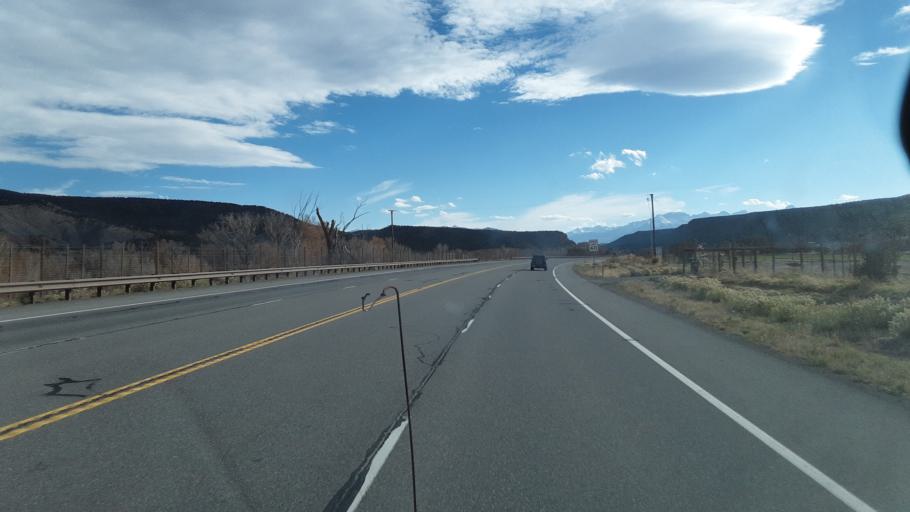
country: US
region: Colorado
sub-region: Montrose County
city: Montrose
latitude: 38.3213
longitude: -107.7758
